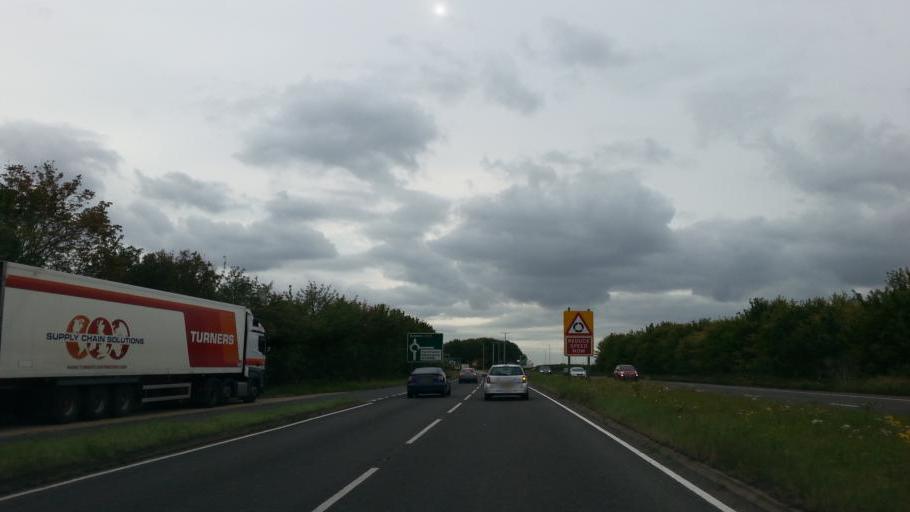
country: GB
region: England
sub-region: Hertfordshire
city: Royston
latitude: 52.0628
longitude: -0.0254
